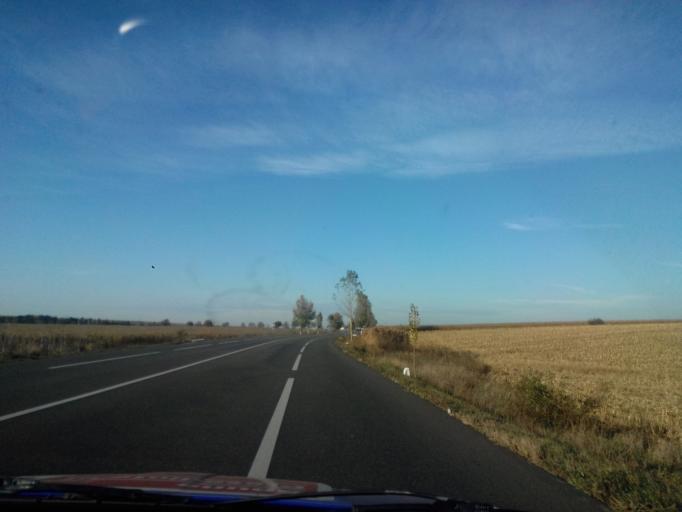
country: RO
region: Bacau
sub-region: Comuna Itesti
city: Itesti
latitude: 46.6914
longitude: 26.8944
